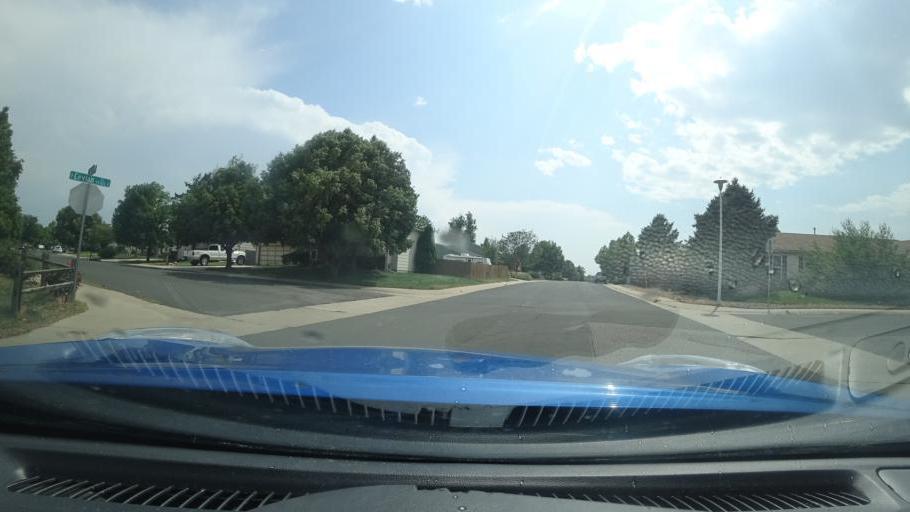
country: US
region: Colorado
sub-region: Adams County
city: Aurora
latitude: 39.6954
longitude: -104.7651
